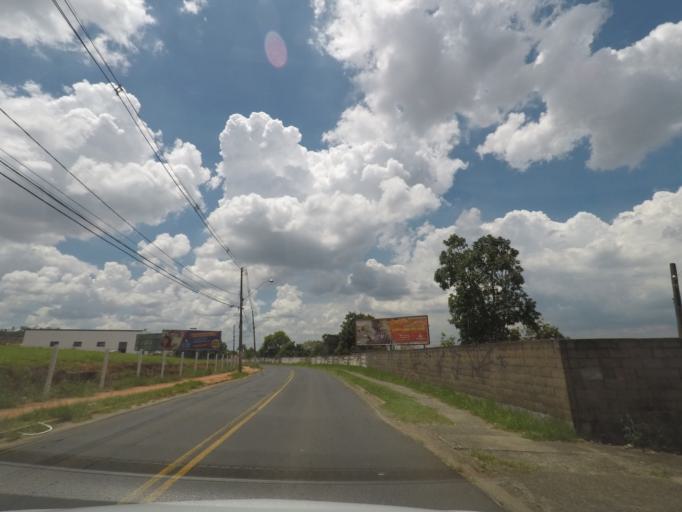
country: BR
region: Sao Paulo
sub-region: Valinhos
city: Valinhos
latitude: -22.9534
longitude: -46.9978
